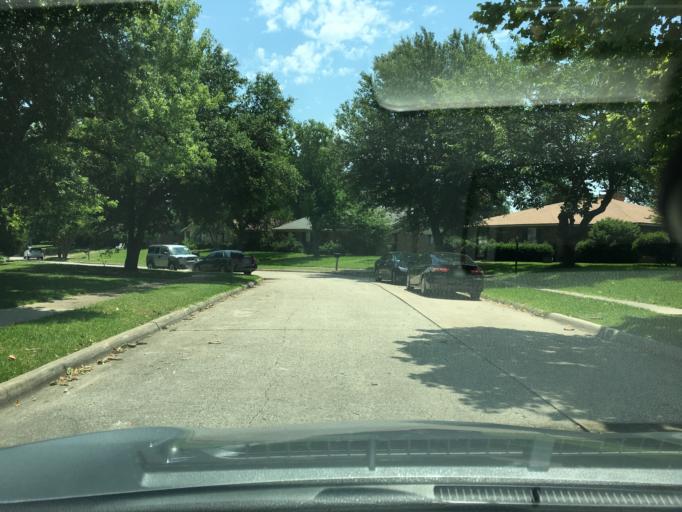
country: US
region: Texas
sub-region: Dallas County
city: Richardson
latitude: 32.9662
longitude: -96.6858
